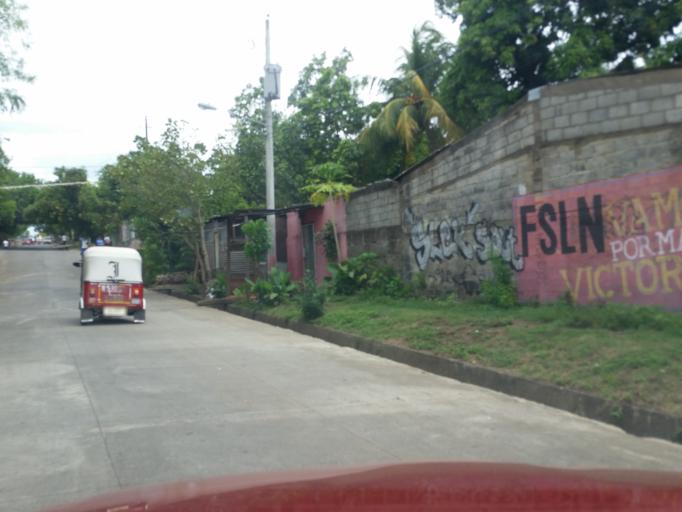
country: NI
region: Managua
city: Managua
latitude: 12.1053
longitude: -86.2272
